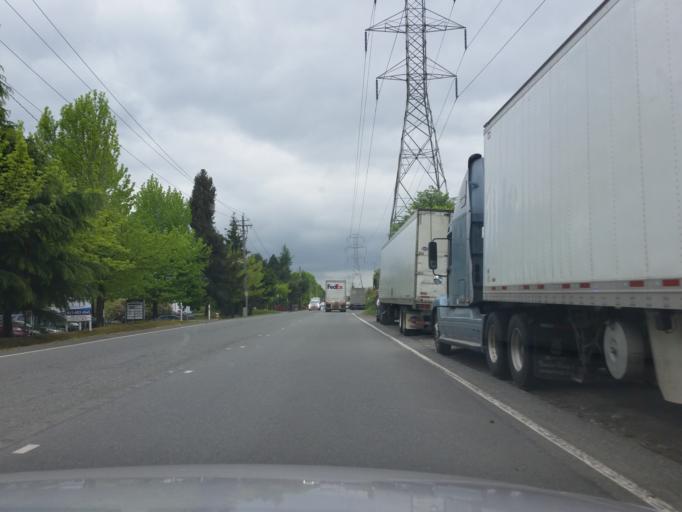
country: US
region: Washington
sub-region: King County
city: Bellevue
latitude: 47.6253
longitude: -122.1751
